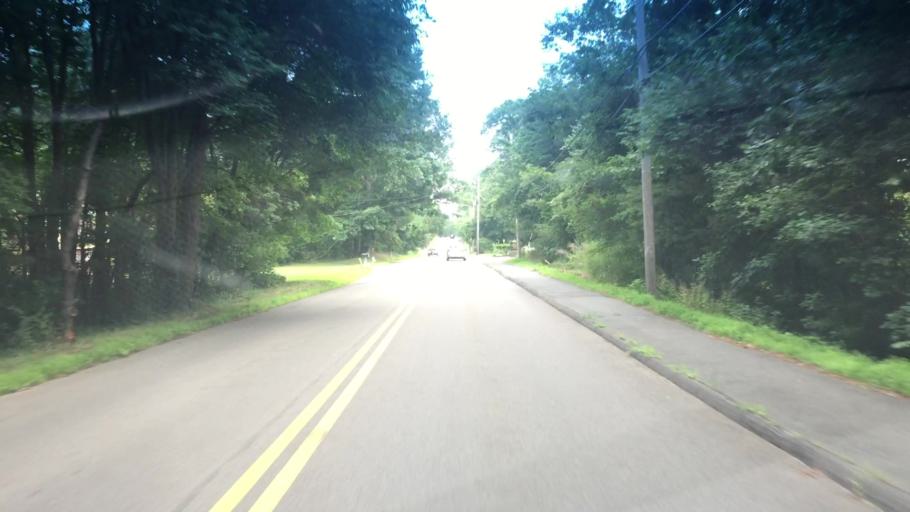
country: US
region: Massachusetts
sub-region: Norfolk County
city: Medway
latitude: 42.1218
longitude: -71.3976
